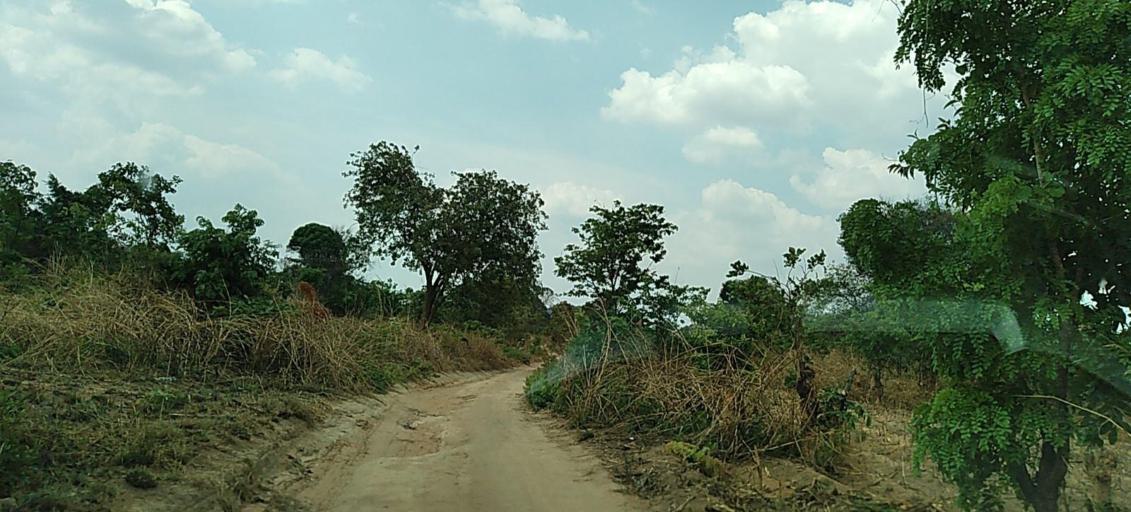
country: ZM
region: Copperbelt
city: Chililabombwe
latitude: -12.3223
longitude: 27.7486
